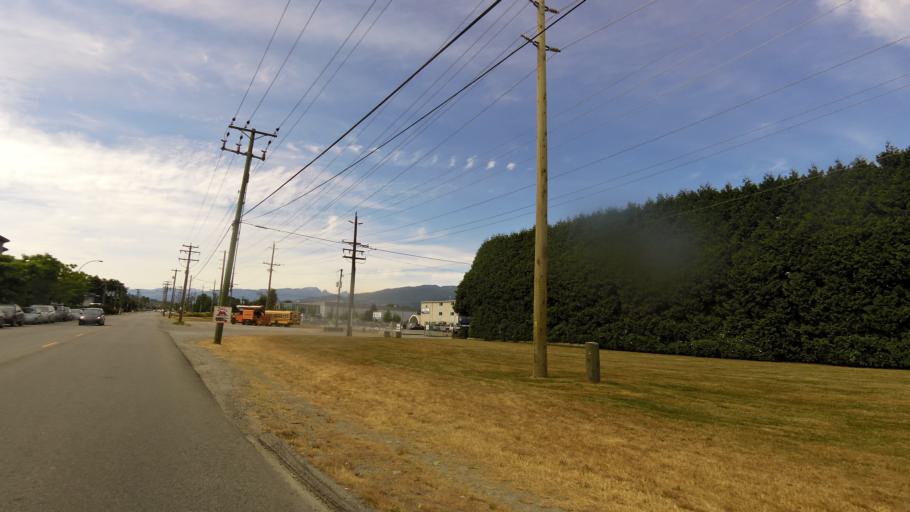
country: CA
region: British Columbia
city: Coquitlam
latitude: 49.2503
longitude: -122.7564
